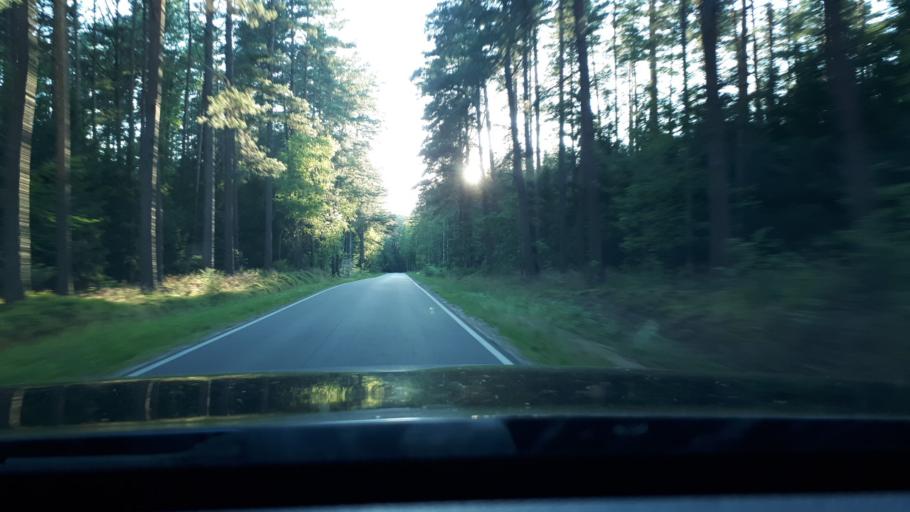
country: PL
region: Warmian-Masurian Voivodeship
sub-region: Powiat olsztynski
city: Stawiguda
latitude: 53.5884
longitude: 20.4416
